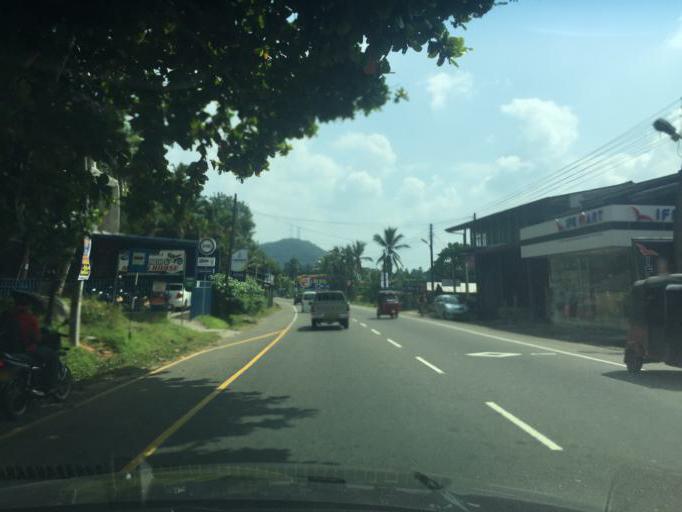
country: LK
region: Western
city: Horana South
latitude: 6.7202
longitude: 80.0492
